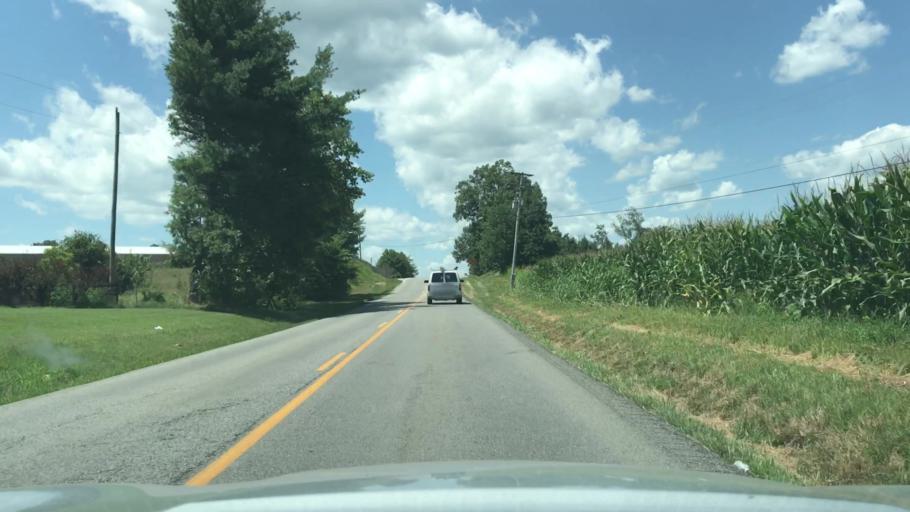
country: US
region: Kentucky
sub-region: Christian County
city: Hopkinsville
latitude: 36.8908
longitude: -87.4612
